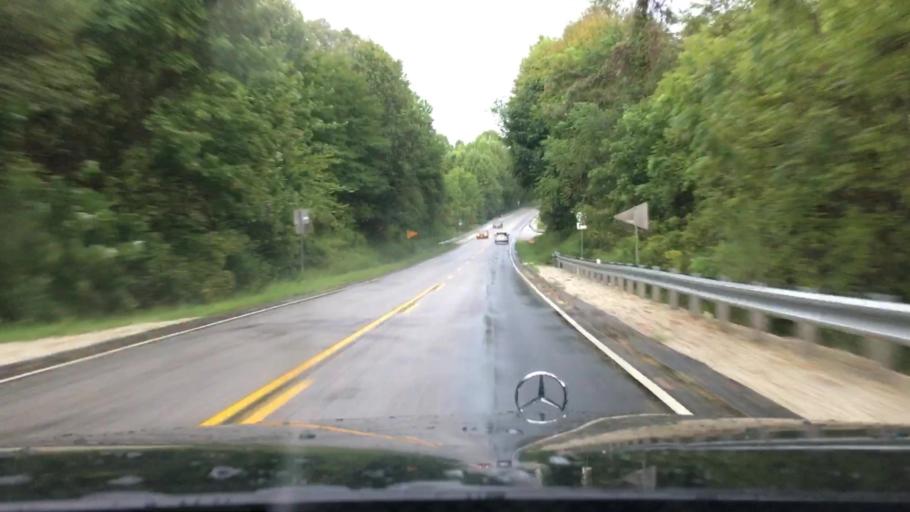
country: US
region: Virginia
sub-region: Amherst County
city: Amherst
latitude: 37.6925
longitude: -79.0279
